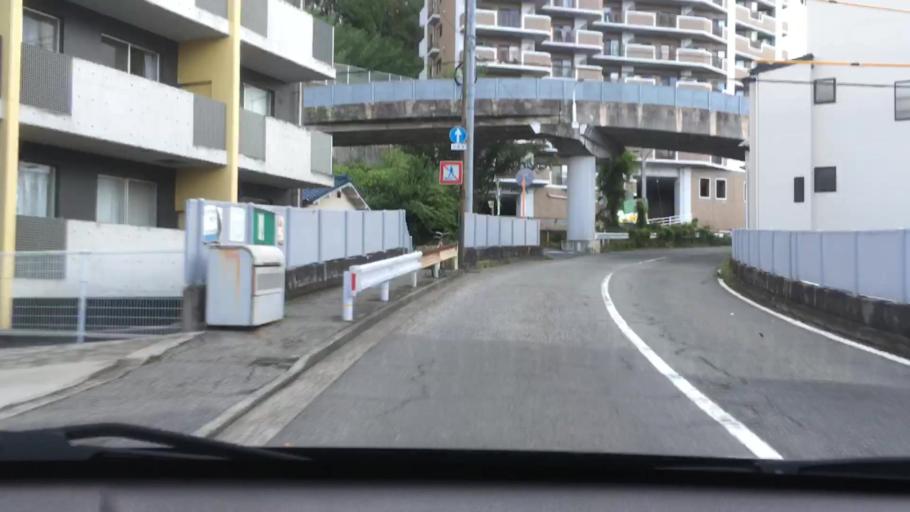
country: JP
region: Hiroshima
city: Hiroshima-shi
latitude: 34.4001
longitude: 132.4295
